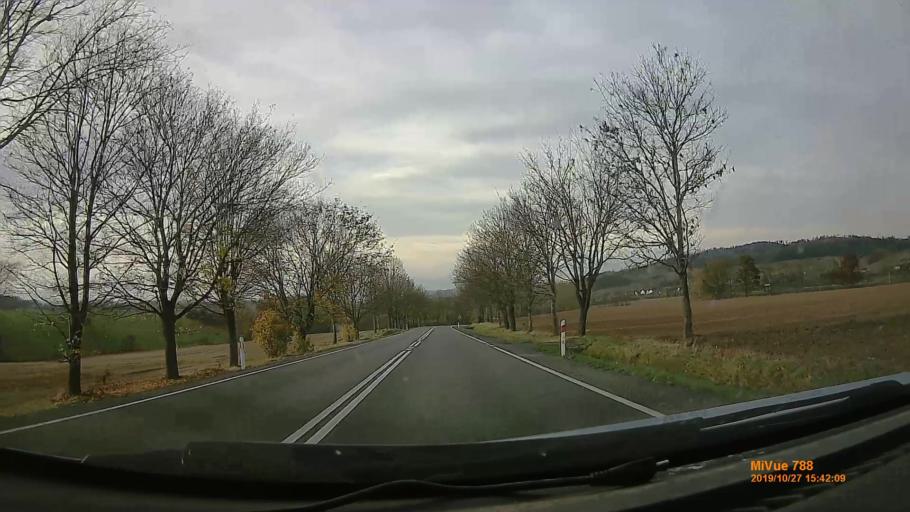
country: PL
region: Lower Silesian Voivodeship
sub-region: Powiat klodzki
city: Klodzko
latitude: 50.4560
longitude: 16.6308
